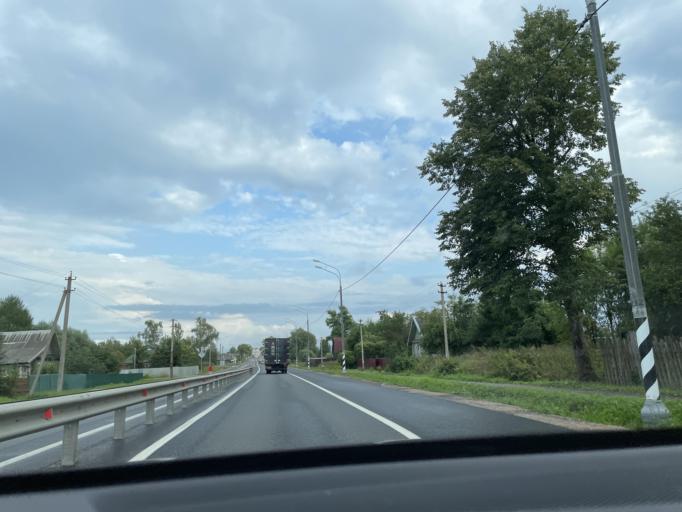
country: RU
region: Tverskaya
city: Kuzhenkino
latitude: 57.7279
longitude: 34.0628
